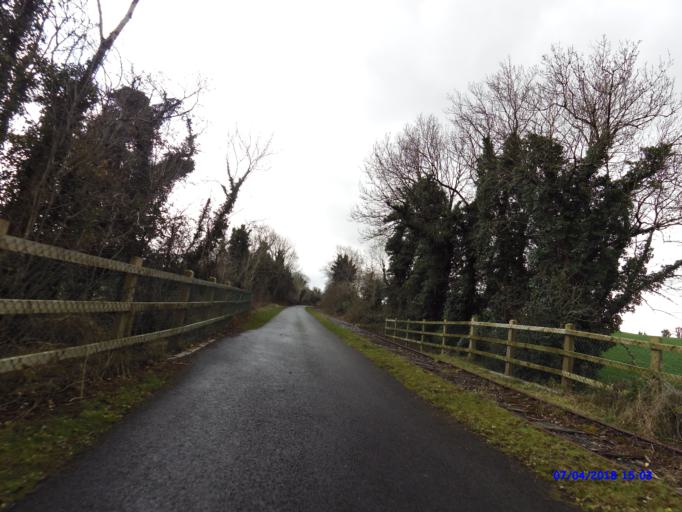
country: IE
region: Leinster
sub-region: An Iarmhi
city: Athlone
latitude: 53.4103
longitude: -7.8368
